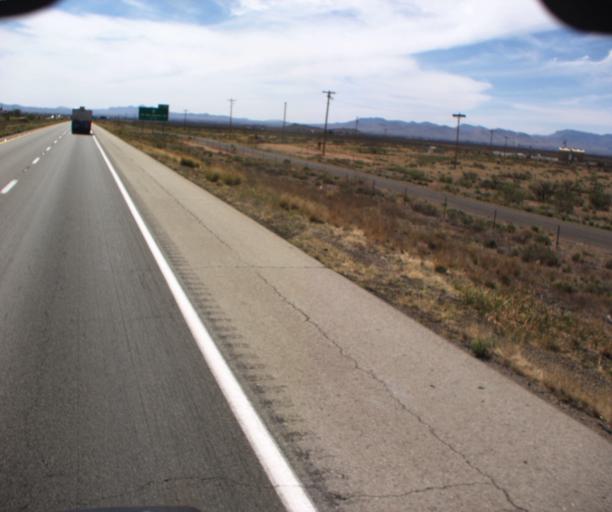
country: US
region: Arizona
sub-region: Cochise County
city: Willcox
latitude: 32.3194
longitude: -109.7823
